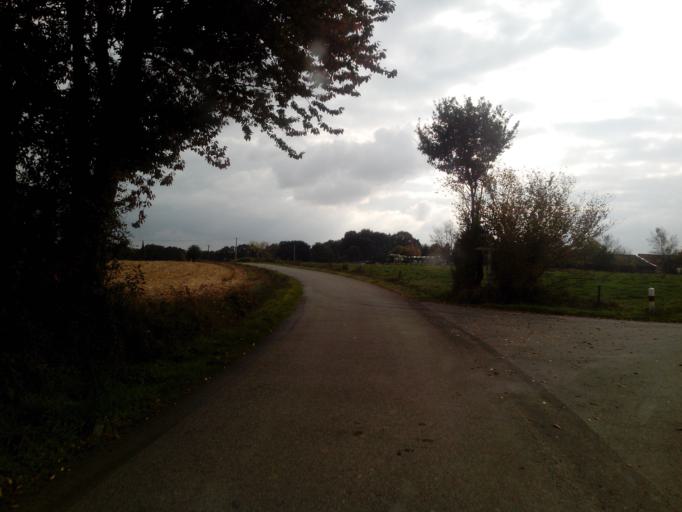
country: FR
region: Brittany
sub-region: Departement du Morbihan
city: Guilliers
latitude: 48.1123
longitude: -2.3833
